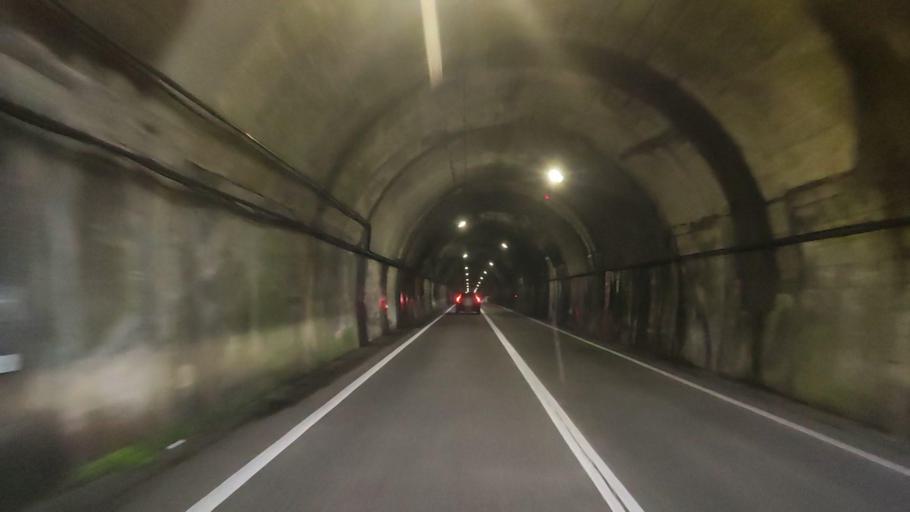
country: JP
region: Mie
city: Ise
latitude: 34.4578
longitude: 136.7363
